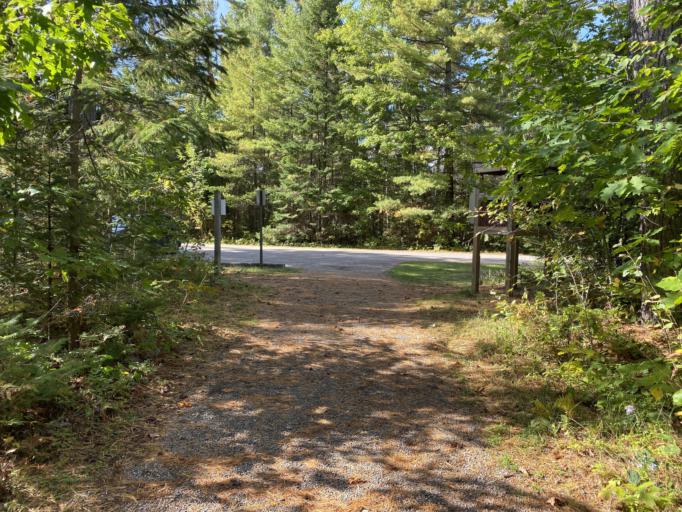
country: US
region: Michigan
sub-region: Mackinac County
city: Saint Ignace
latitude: 45.7434
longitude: -84.8994
